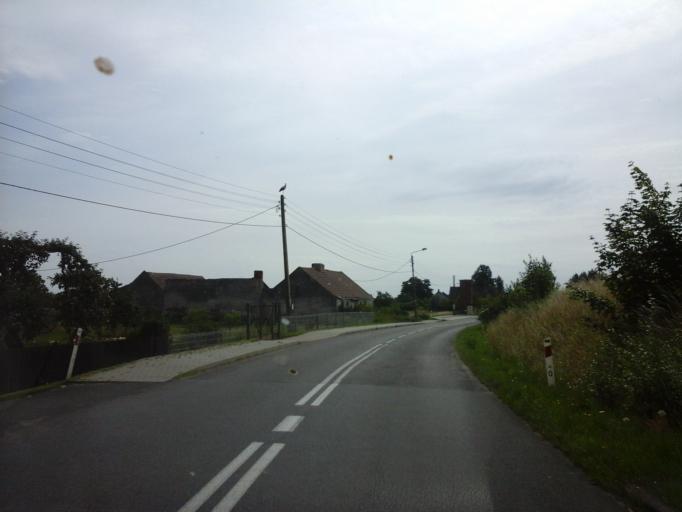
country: PL
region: West Pomeranian Voivodeship
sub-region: Powiat choszczenski
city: Bierzwnik
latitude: 53.0218
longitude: 15.6973
